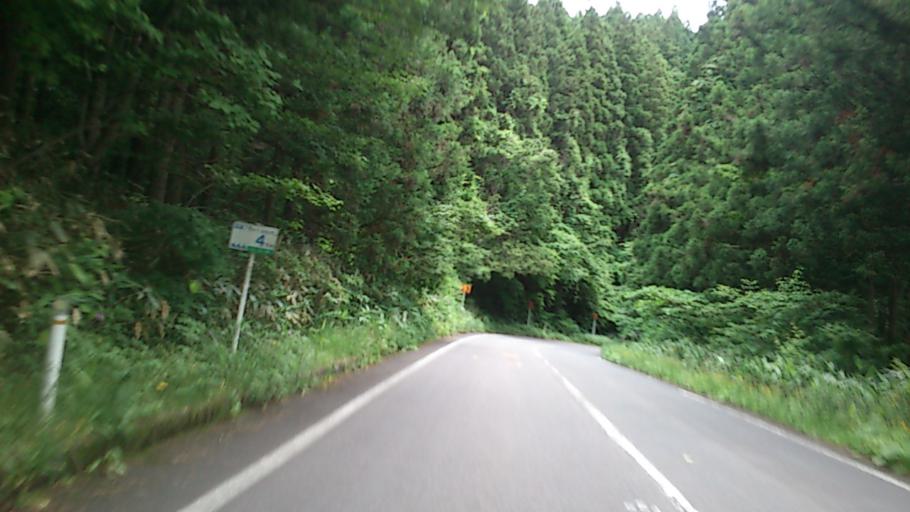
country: JP
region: Yamagata
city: Yuza
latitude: 39.0919
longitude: 139.9081
